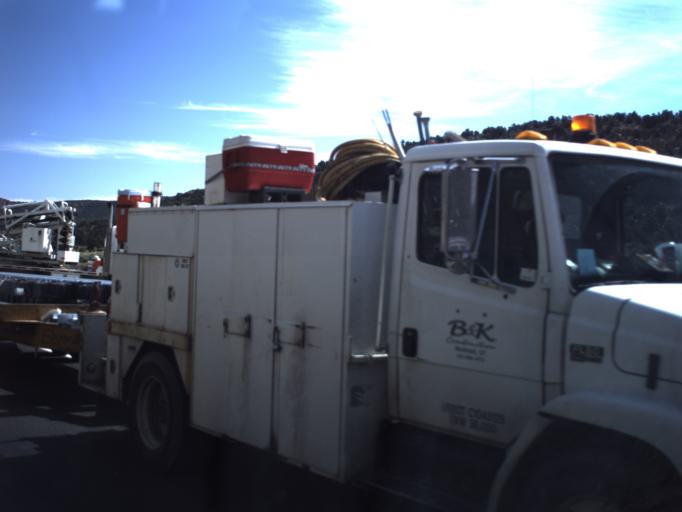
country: US
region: Utah
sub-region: Wayne County
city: Loa
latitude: 37.7346
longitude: -111.7514
